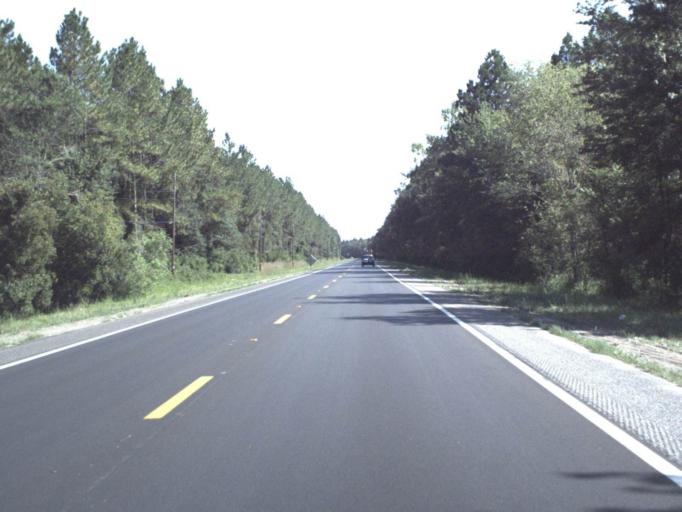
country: US
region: Florida
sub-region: Alachua County
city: Alachua
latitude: 29.7307
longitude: -82.3539
